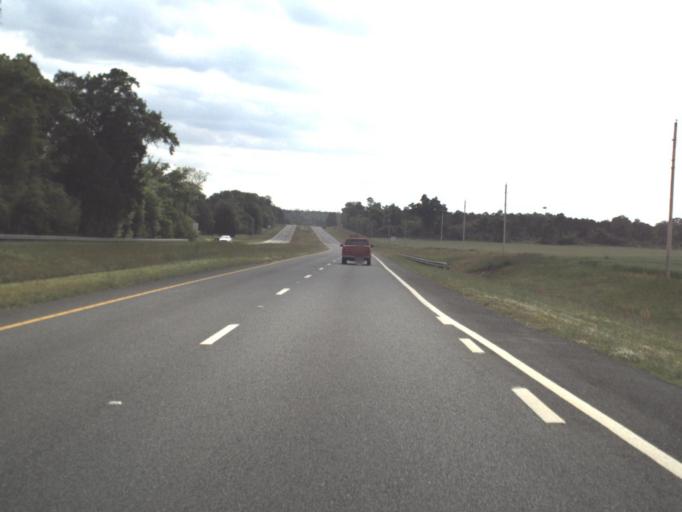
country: US
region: Florida
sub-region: Escambia County
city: Century
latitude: 30.9304
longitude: -87.3017
